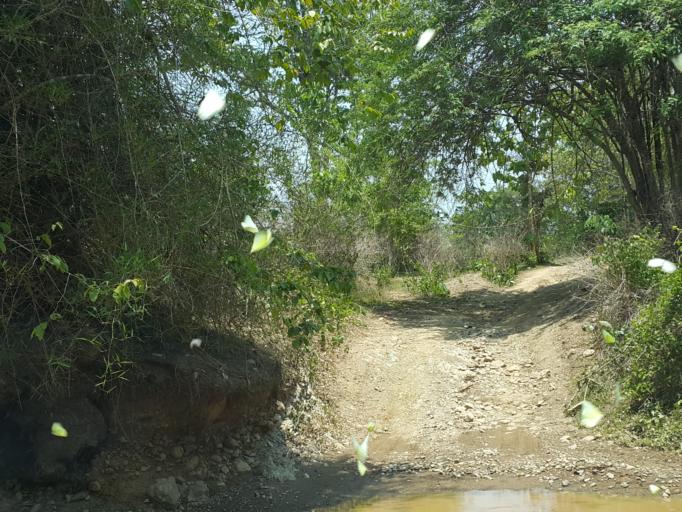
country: TH
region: Kanchanaburi
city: Sai Yok
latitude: 14.2341
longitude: 98.8608
